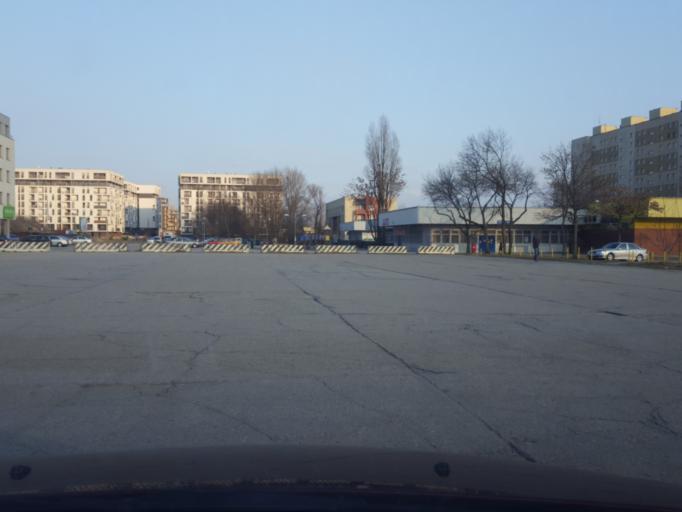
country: PL
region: Lesser Poland Voivodeship
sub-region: Krakow
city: Krakow
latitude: 50.0800
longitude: 20.0094
